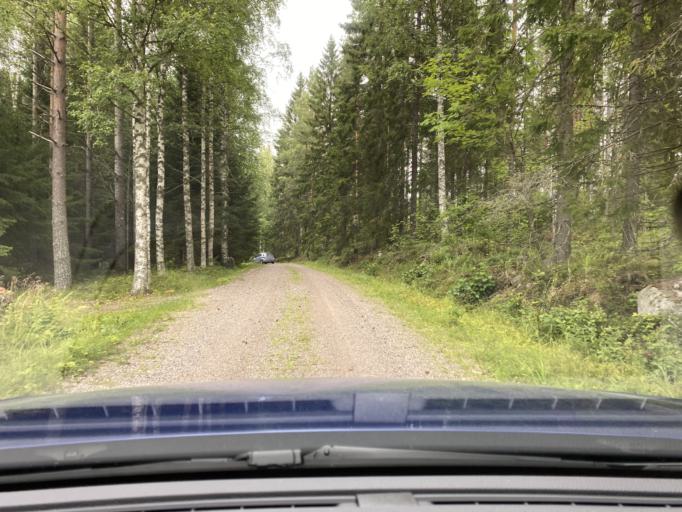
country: FI
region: Pirkanmaa
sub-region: Ylae-Pirkanmaa
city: Maenttae
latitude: 62.0186
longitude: 24.7568
